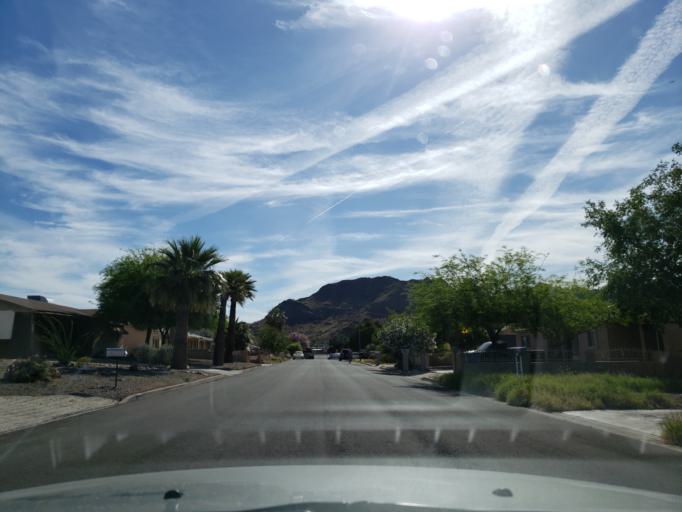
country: US
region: Arizona
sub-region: Maricopa County
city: Paradise Valley
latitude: 33.5830
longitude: -112.0555
